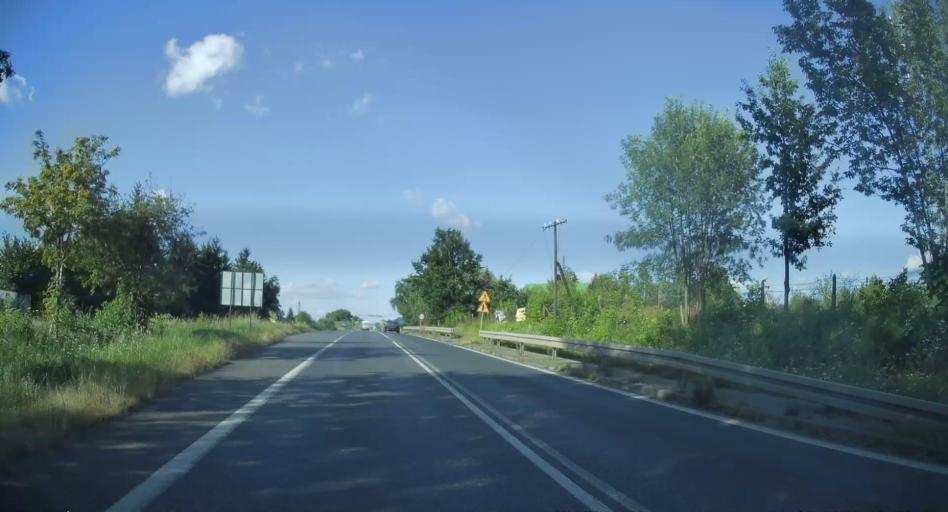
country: PL
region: Masovian Voivodeship
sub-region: Powiat grojecki
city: Grojec
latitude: 51.8573
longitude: 20.8501
